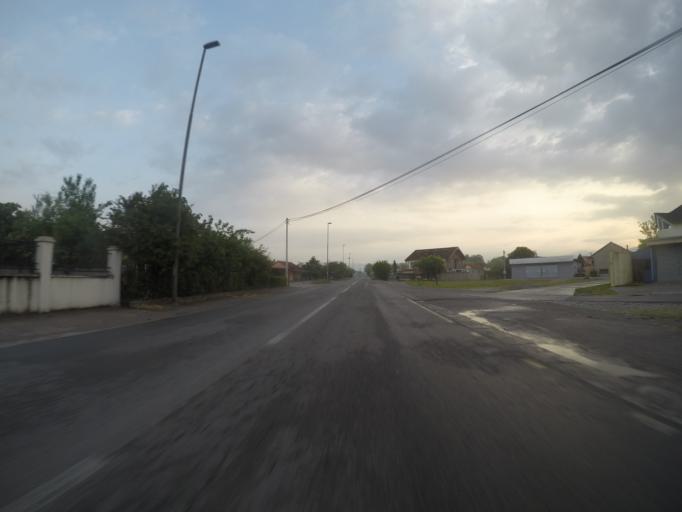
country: ME
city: Mojanovici
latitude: 42.3416
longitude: 19.2216
